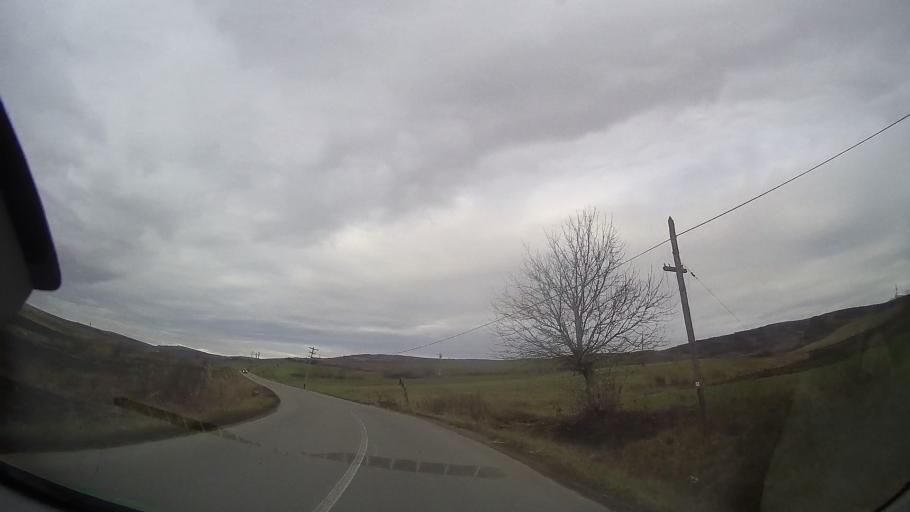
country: RO
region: Mures
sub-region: Comuna Faragau
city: Faragau
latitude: 46.7417
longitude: 24.5373
